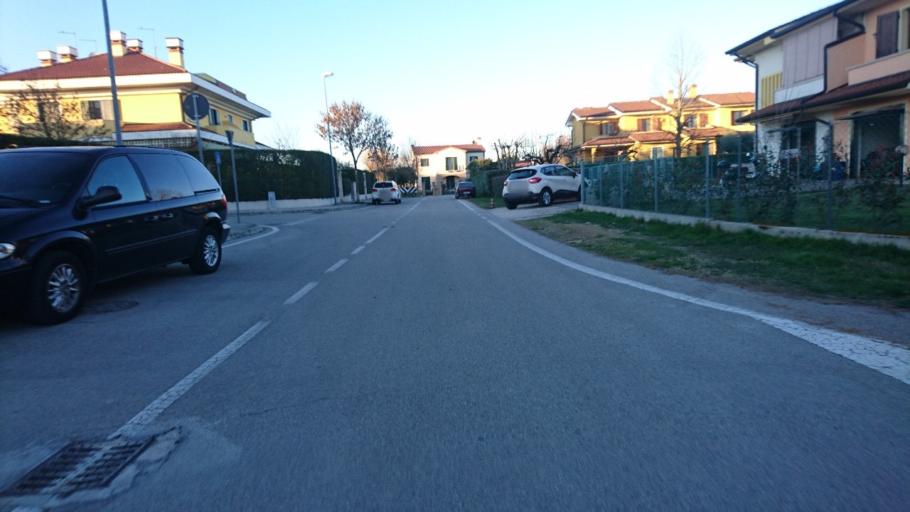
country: IT
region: Veneto
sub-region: Provincia di Padova
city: Albignasego
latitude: 45.3412
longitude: 11.9075
